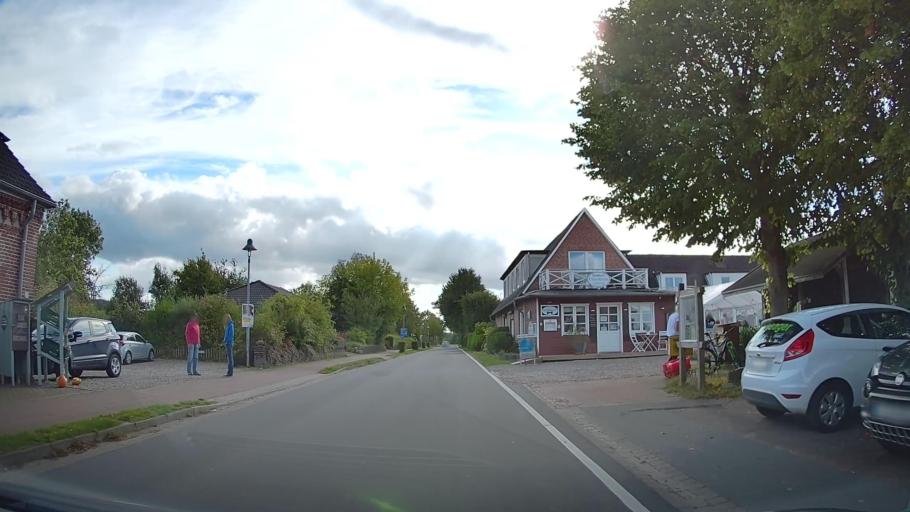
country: DE
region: Schleswig-Holstein
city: Westerholz
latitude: 54.8161
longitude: 9.6719
